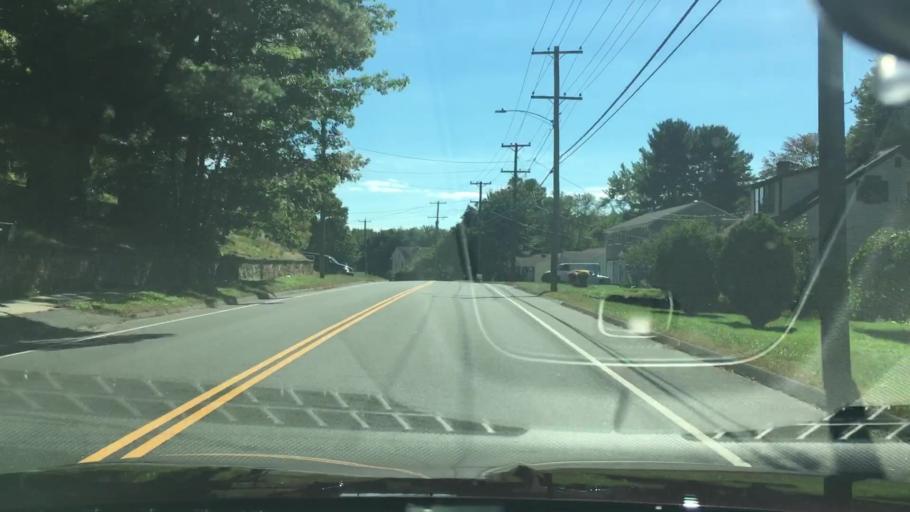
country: US
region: Connecticut
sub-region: Hartford County
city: Bristol
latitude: 41.6877
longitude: -72.9117
